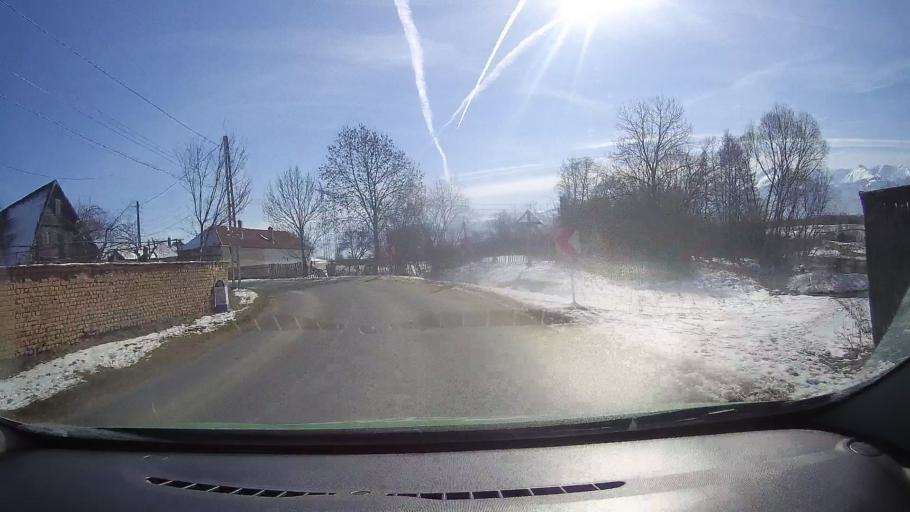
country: RO
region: Brasov
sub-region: Comuna Sambata de Sus
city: Sambata de Sus
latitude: 45.7552
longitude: 24.8318
